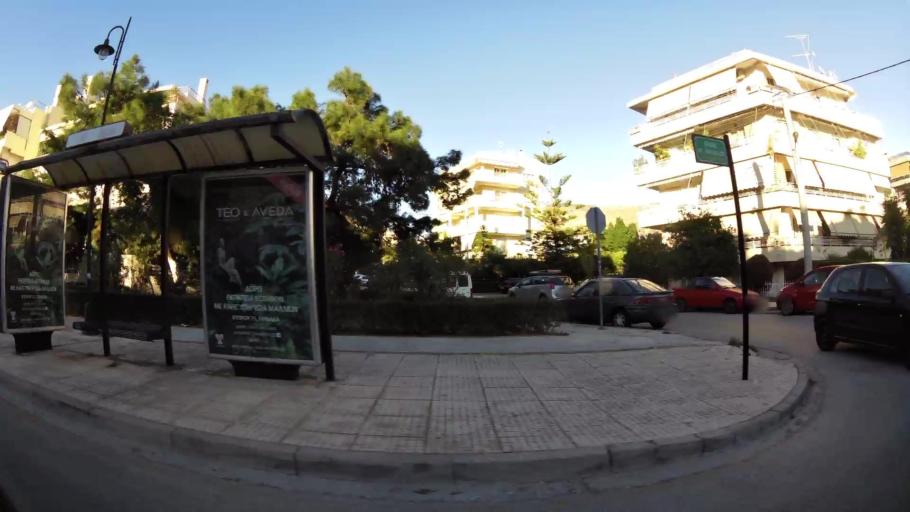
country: GR
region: Attica
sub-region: Nomarchia Athinas
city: Glyfada
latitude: 37.8657
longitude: 23.7584
